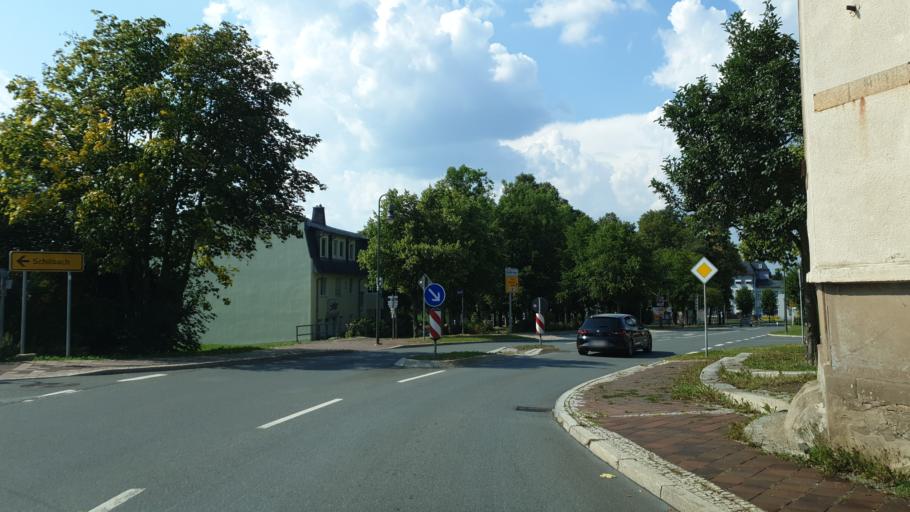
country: DE
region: Saxony
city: Pohl
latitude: 50.3955
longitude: 12.3386
